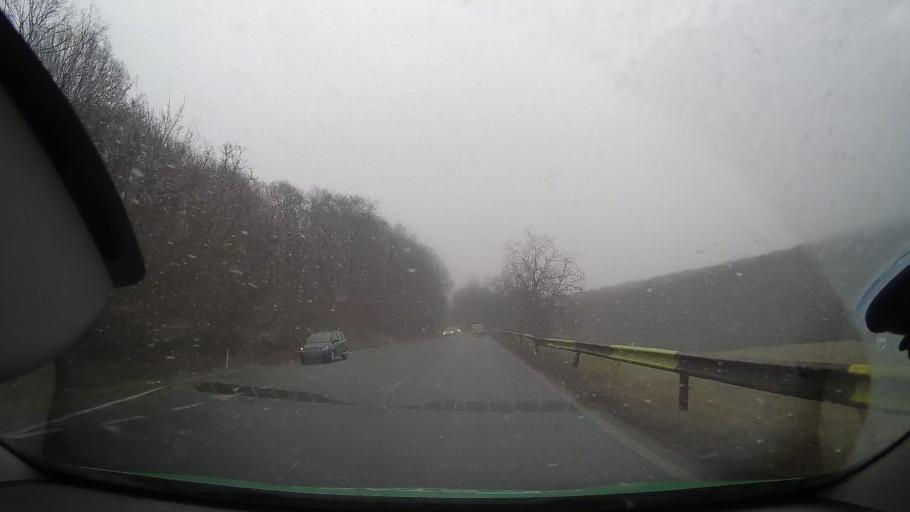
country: RO
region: Sibiu
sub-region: Comuna Blajel
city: Blajel
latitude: 46.1904
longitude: 24.3261
